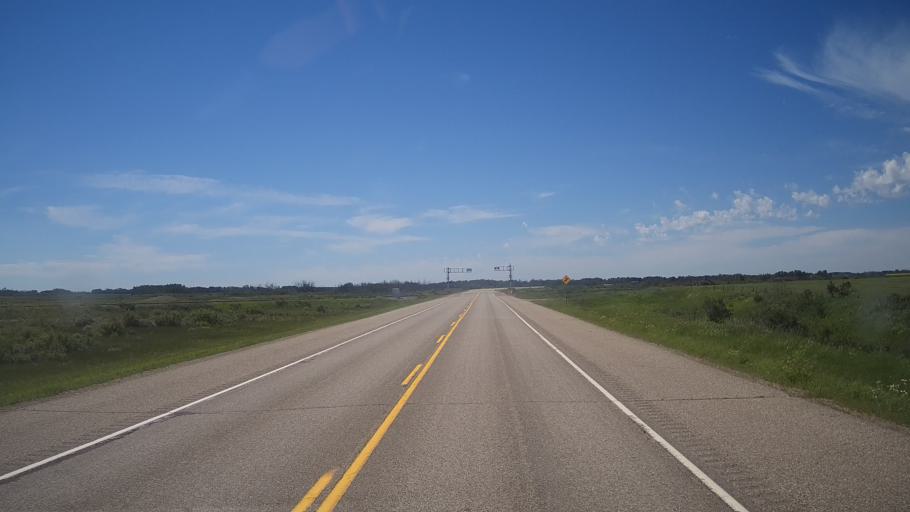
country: CA
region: Saskatchewan
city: Langenburg
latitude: 50.7715
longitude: -101.4875
